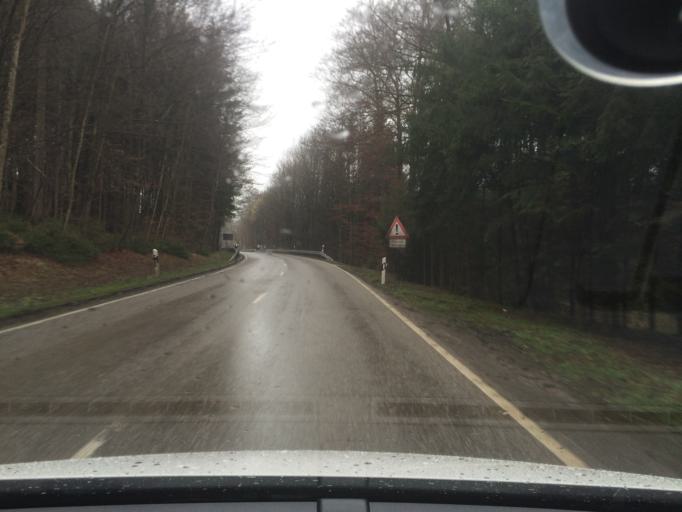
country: DE
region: Bavaria
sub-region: Upper Bavaria
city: Assling
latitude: 47.9800
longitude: 11.9511
